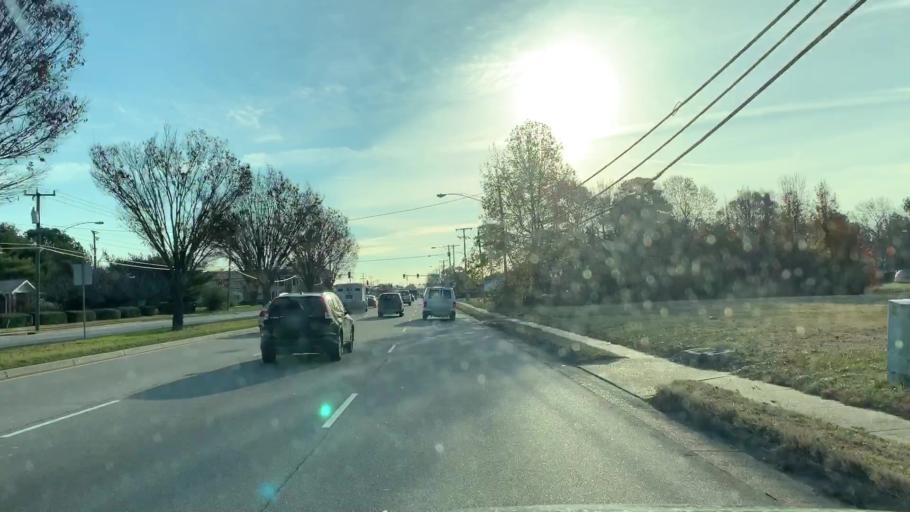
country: US
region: Virginia
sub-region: City of Chesapeake
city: Chesapeake
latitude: 36.8017
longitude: -76.1837
